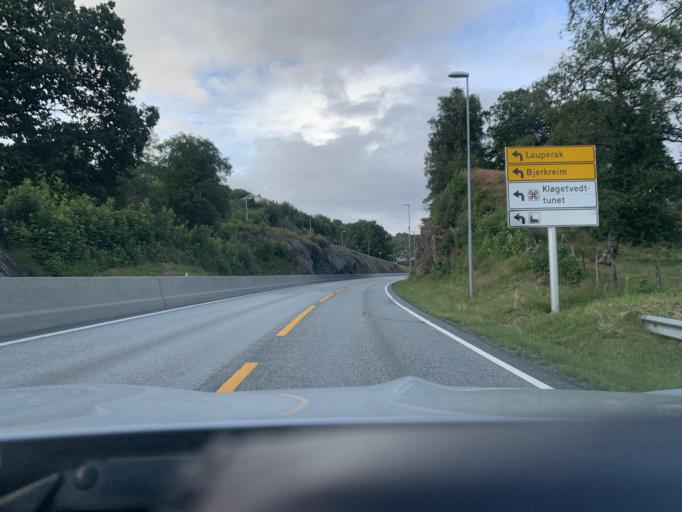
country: NO
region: Rogaland
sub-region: Bjerkreim
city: Vikesa
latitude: 58.5818
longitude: 6.0640
